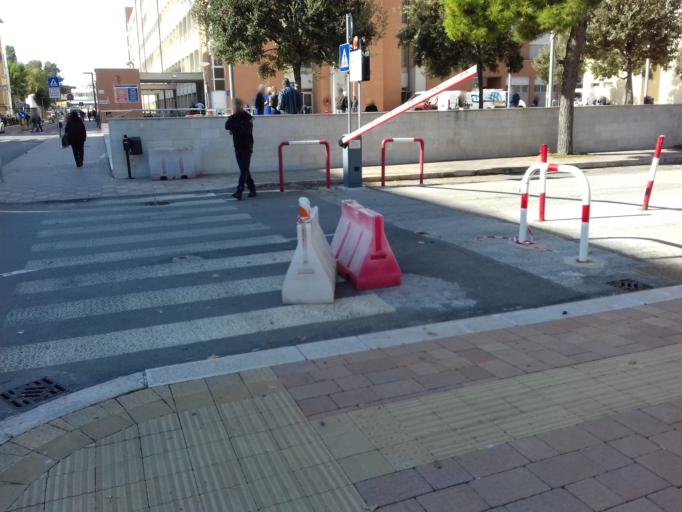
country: IT
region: Apulia
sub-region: Provincia di Bari
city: Bari
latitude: 41.1130
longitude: 16.8596
